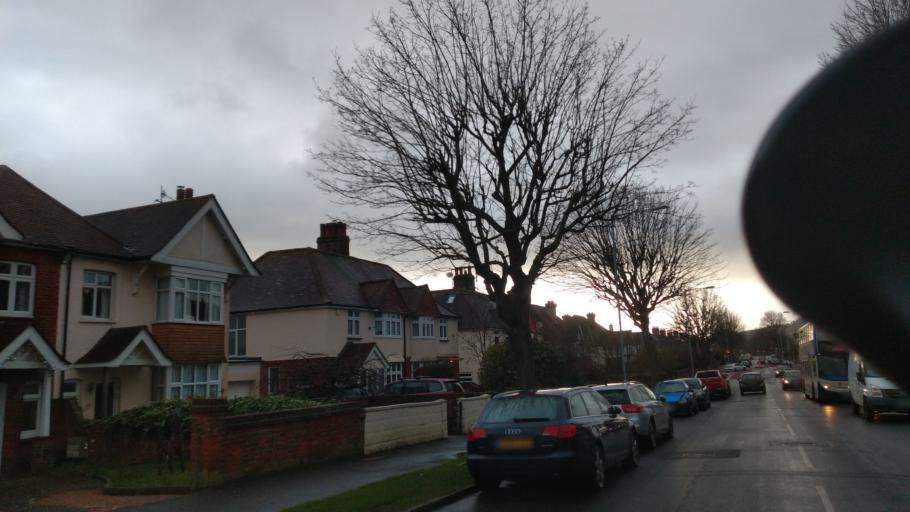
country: GB
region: England
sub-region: East Sussex
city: Eastbourne
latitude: 50.7810
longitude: 0.2549
